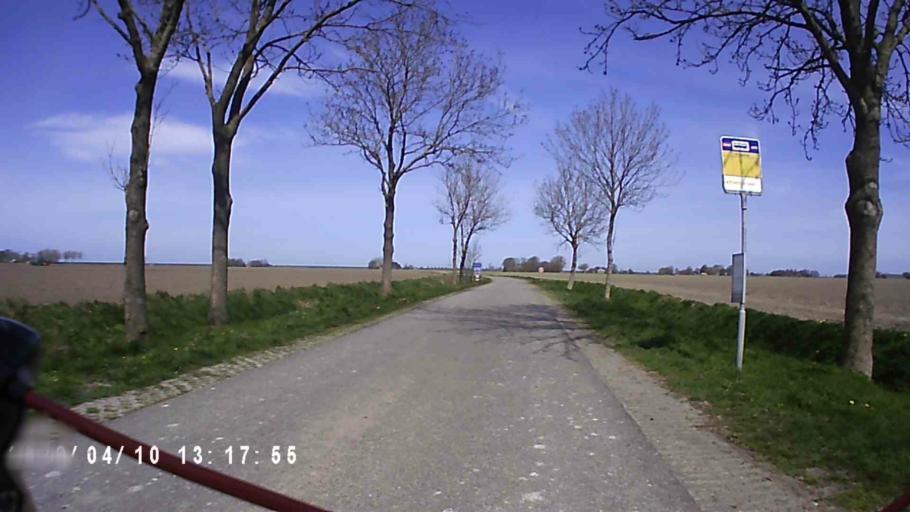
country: NL
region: Groningen
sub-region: Gemeente Zuidhorn
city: Oldehove
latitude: 53.3947
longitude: 6.4244
